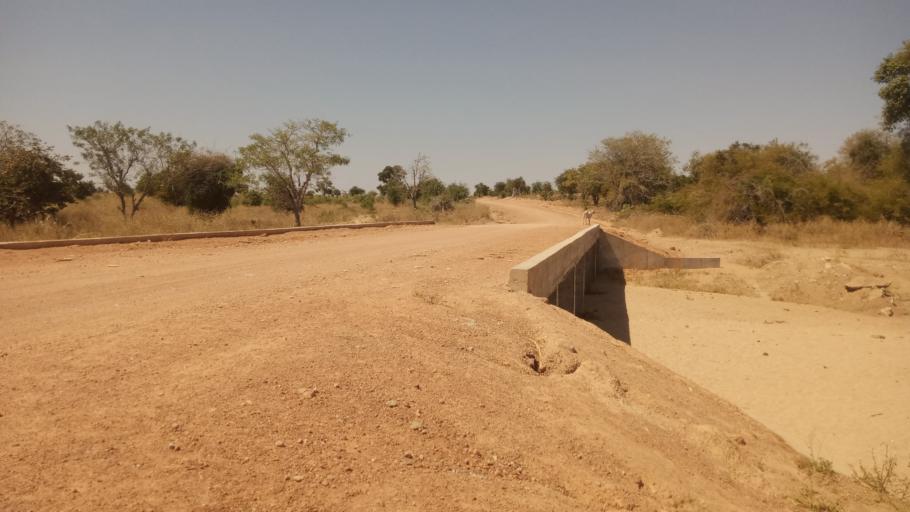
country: NG
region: Borno
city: Shani
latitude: 9.8640
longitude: 12.1196
